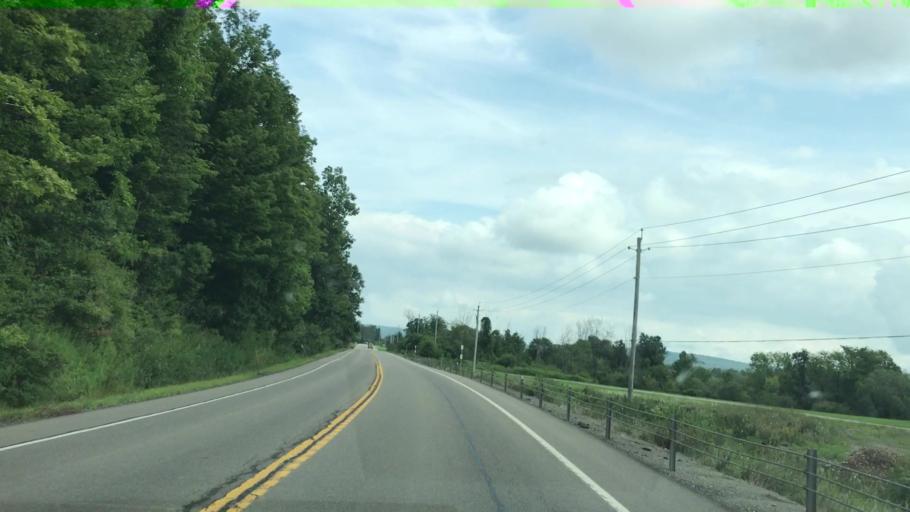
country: US
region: New York
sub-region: Steuben County
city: Bath
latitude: 42.4644
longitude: -77.3019
